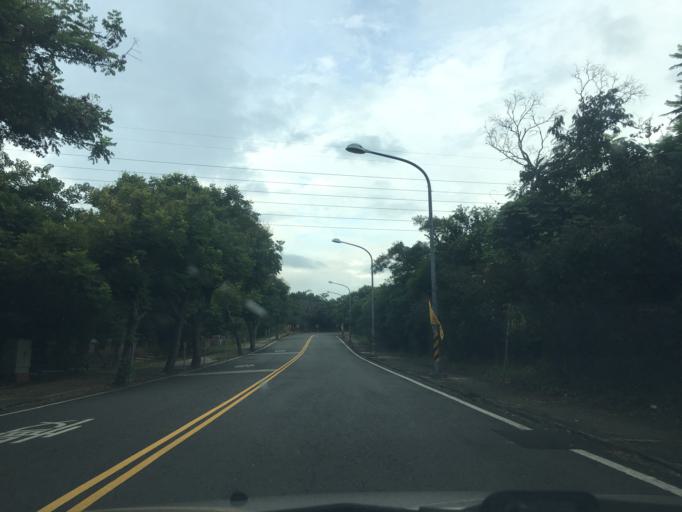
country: TW
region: Taiwan
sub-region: Changhua
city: Chang-hua
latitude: 24.0660
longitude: 120.5685
